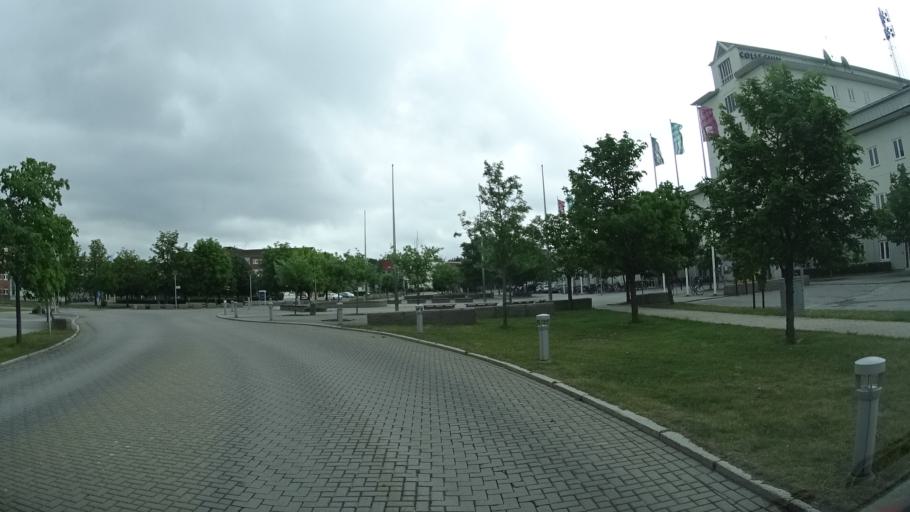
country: SE
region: OEstergoetland
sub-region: Linkopings Kommun
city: Malmslatt
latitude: 58.3939
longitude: 15.5600
